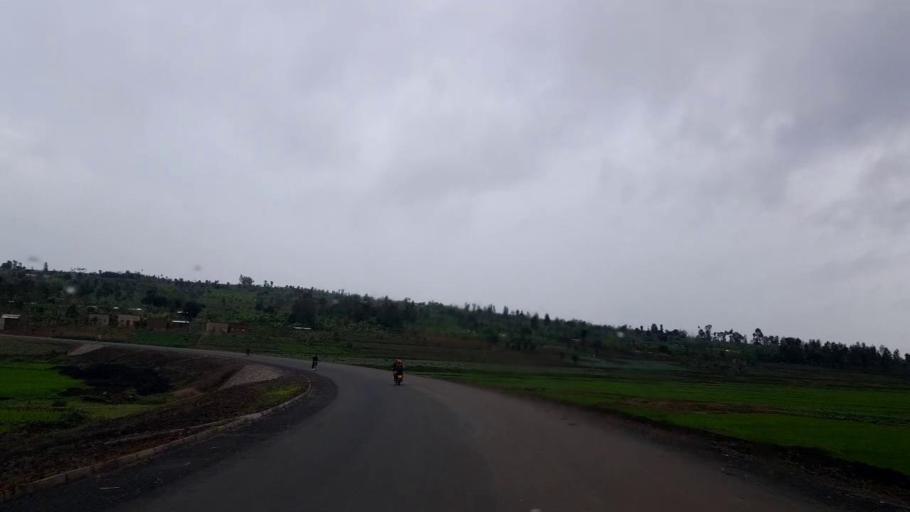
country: RW
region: Northern Province
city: Byumba
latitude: -1.4281
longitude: 30.2735
